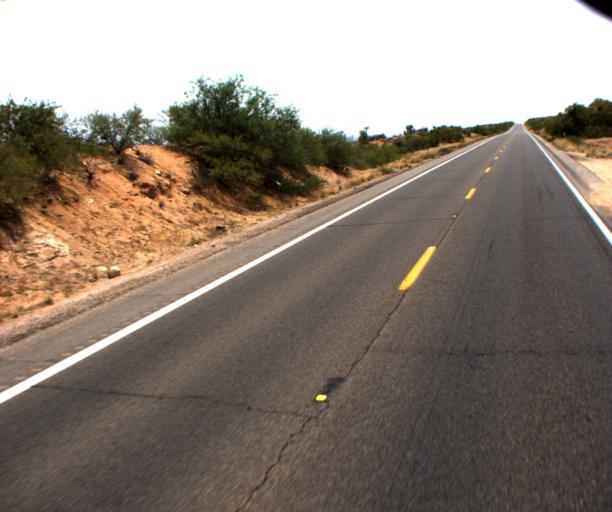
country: US
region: Arizona
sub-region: Gila County
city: Peridot
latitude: 33.3349
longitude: -110.5827
